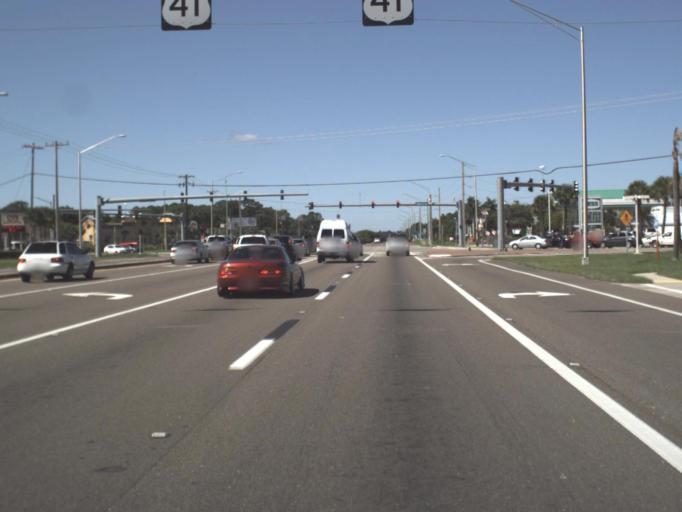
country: US
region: Florida
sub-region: Lee County
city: North Fort Myers
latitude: 26.6664
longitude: -81.8890
